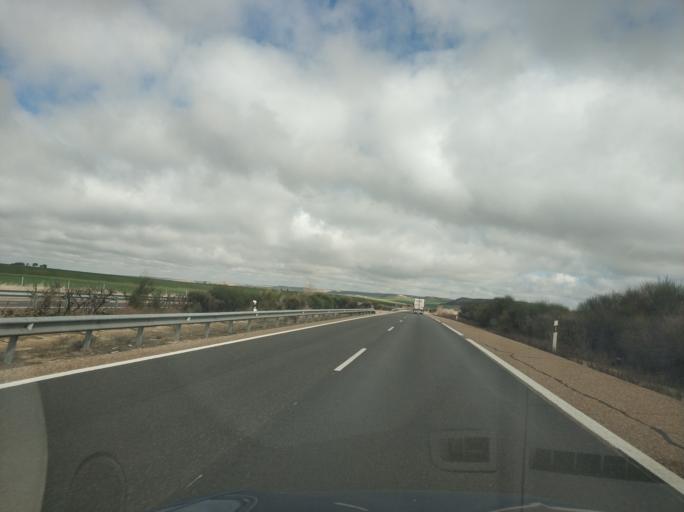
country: ES
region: Castille and Leon
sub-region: Provincia de Zamora
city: Canizal
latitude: 41.1858
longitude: -5.3594
